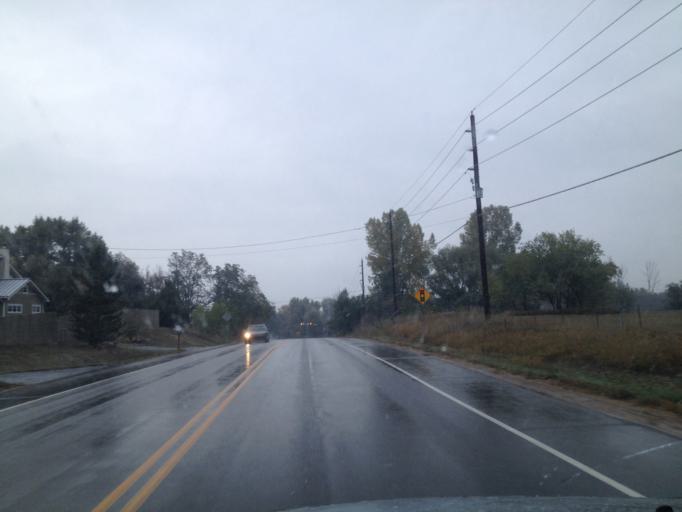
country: US
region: Colorado
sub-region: Boulder County
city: Superior
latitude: 39.9979
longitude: -105.1750
